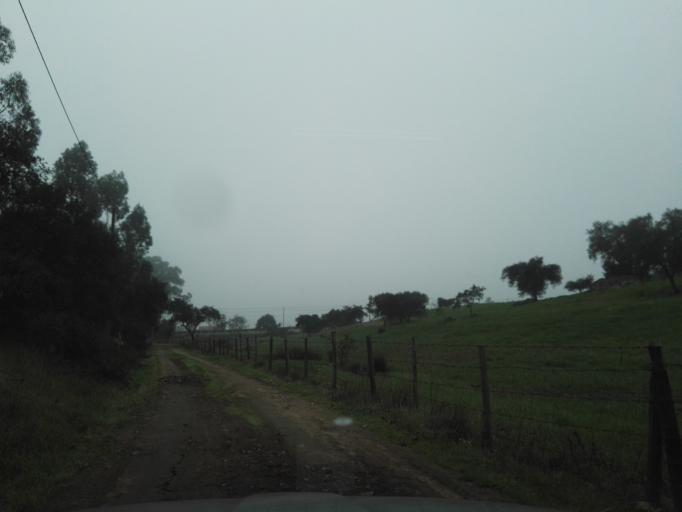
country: PT
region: Evora
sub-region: Montemor-O-Novo
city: Montemor-o-Novo
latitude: 38.7900
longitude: -8.2246
